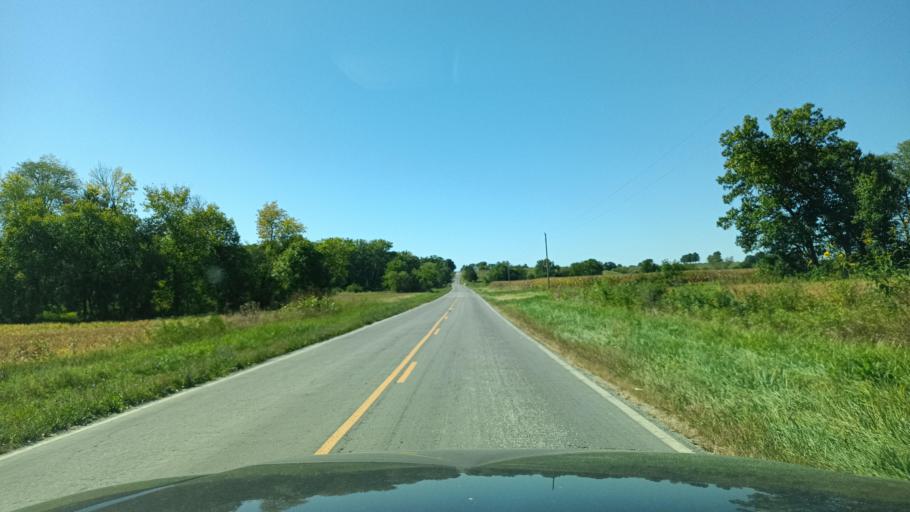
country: US
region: Missouri
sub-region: Macon County
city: La Plata
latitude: 40.0218
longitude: -92.5373
